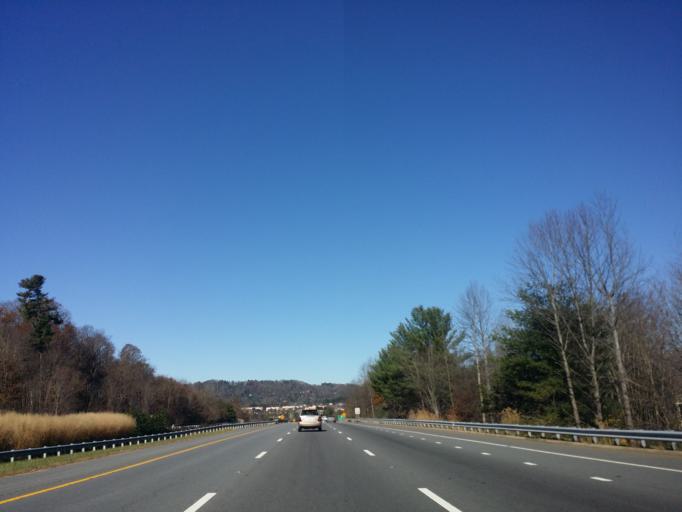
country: US
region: North Carolina
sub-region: Buncombe County
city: Biltmore Forest
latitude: 35.5707
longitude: -82.5111
